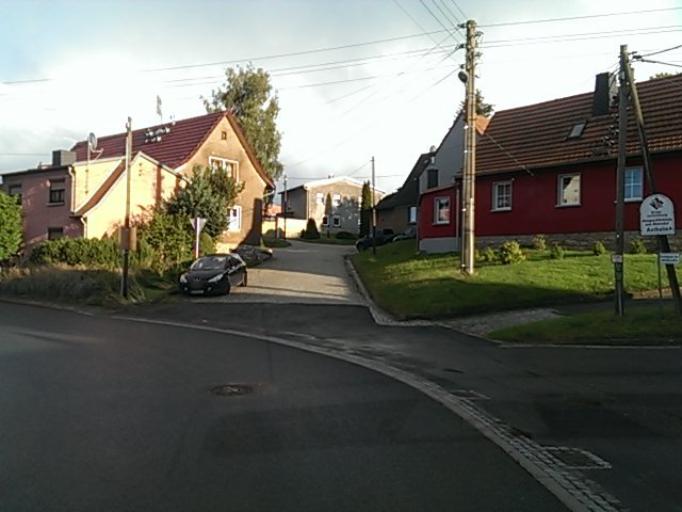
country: DE
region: Thuringia
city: Ostramondra
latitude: 51.1981
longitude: 11.3310
